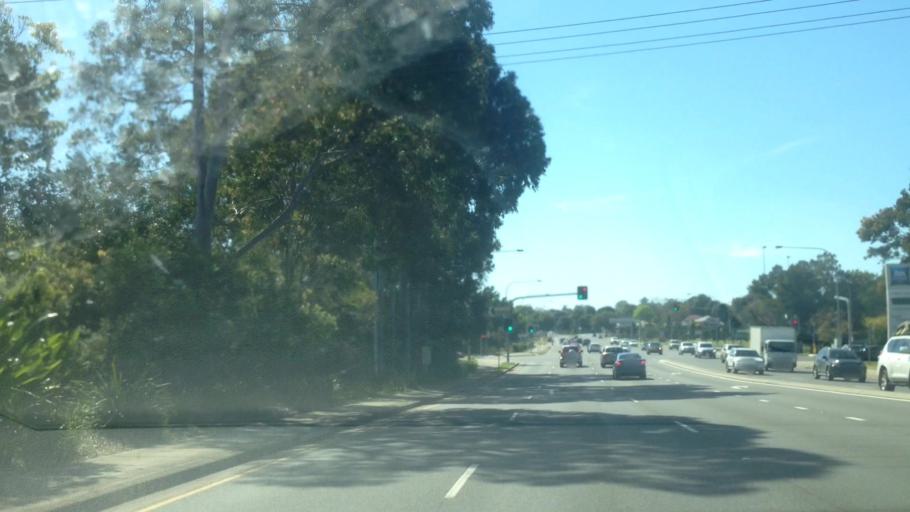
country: AU
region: New South Wales
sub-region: Newcastle
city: Elermore Vale
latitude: -32.9076
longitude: 151.6640
